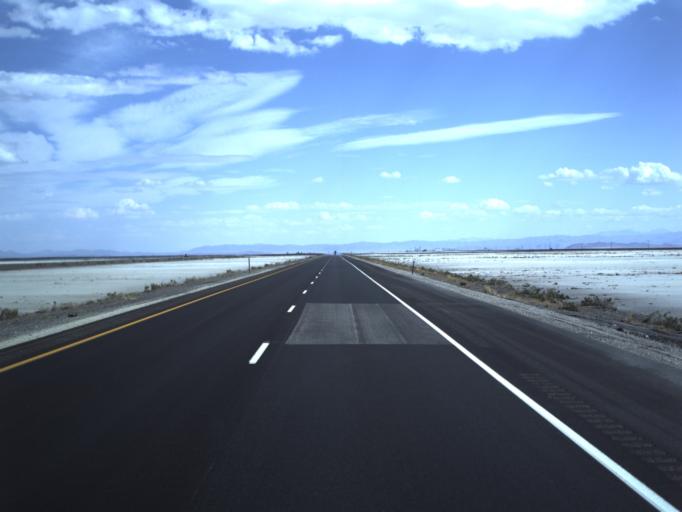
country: US
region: Utah
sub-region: Tooele County
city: Wendover
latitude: 40.7313
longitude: -113.5188
